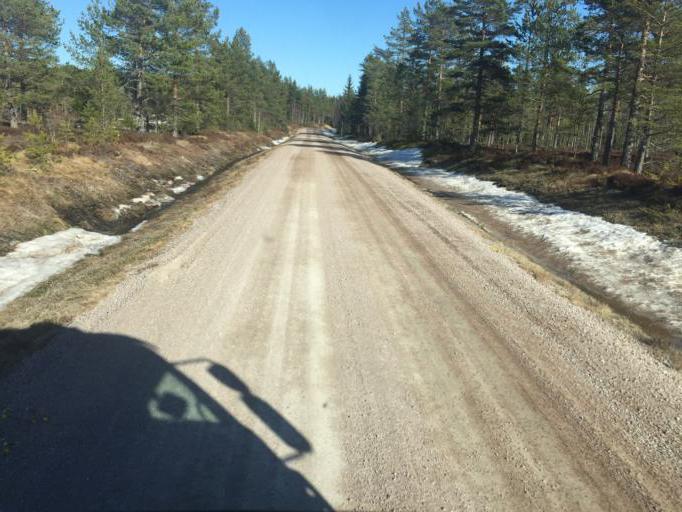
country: SE
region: Vaermland
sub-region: Filipstads Kommun
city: Lesjofors
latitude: 60.2522
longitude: 14.0534
